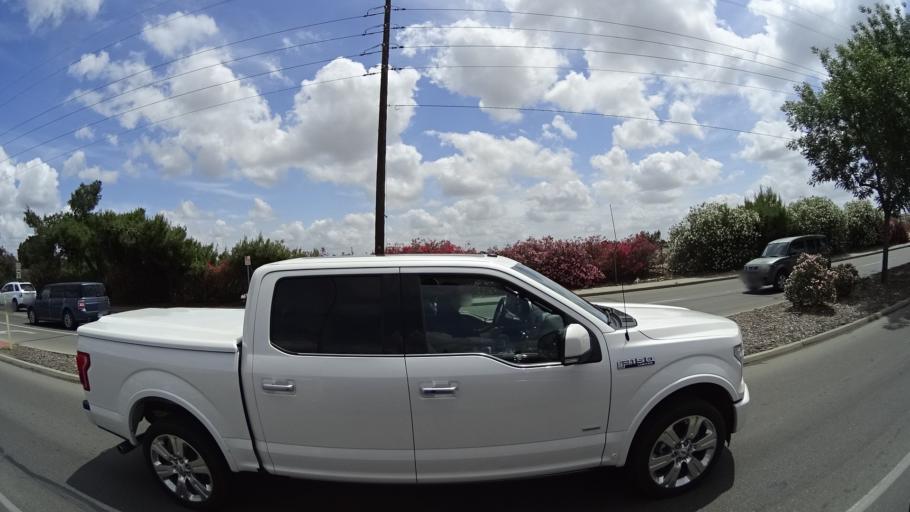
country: US
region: California
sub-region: Kings County
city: Hanford
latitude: 36.3198
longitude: -119.6552
